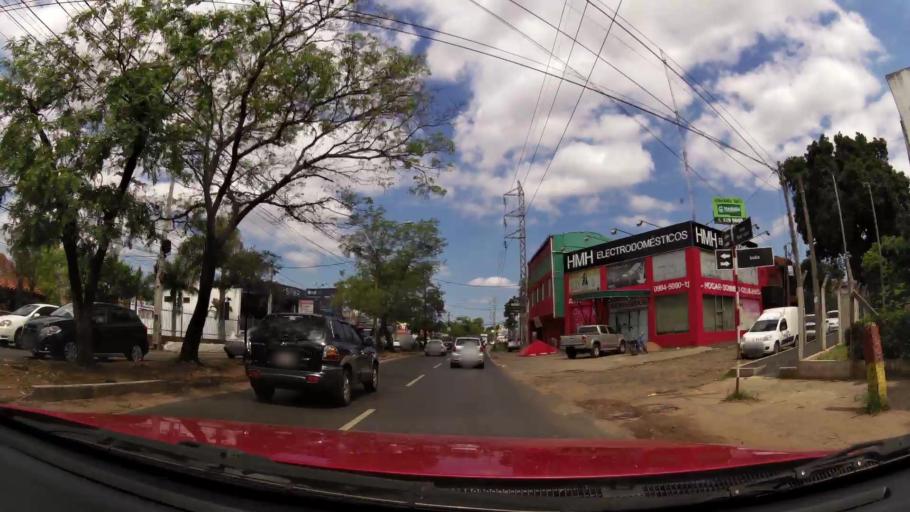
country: PY
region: Central
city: Fernando de la Mora
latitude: -25.3051
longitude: -57.5358
